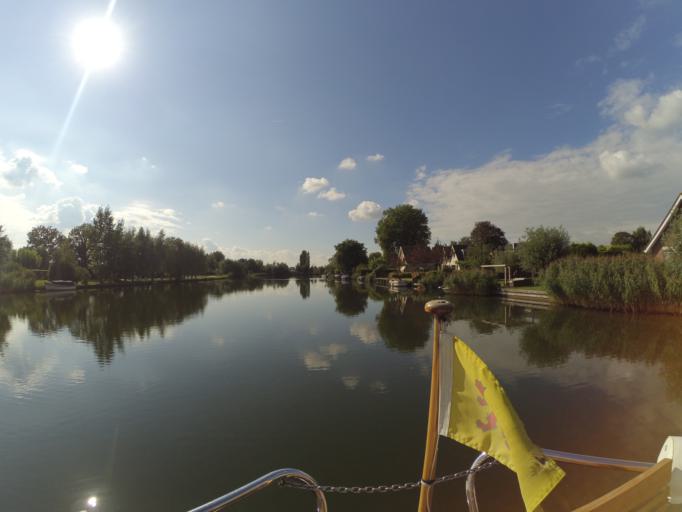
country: NL
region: North Holland
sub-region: Gemeente Weesp
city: Weesp
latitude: 52.2743
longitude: 5.0319
